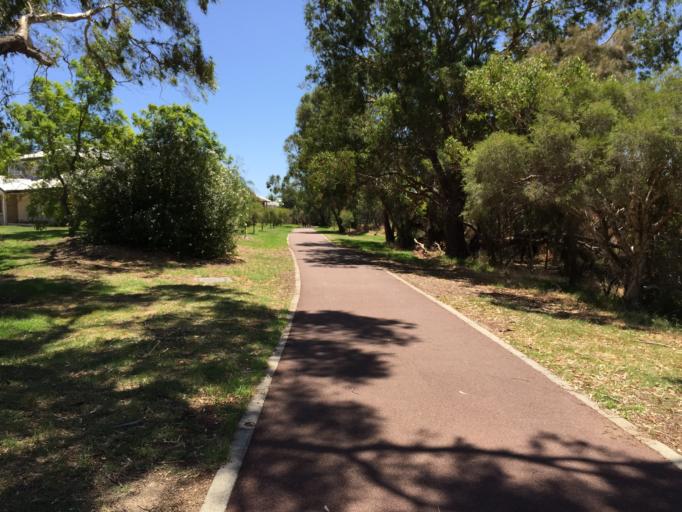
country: AU
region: Western Australia
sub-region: Canning
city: Wilson
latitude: -32.0303
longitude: 115.9020
